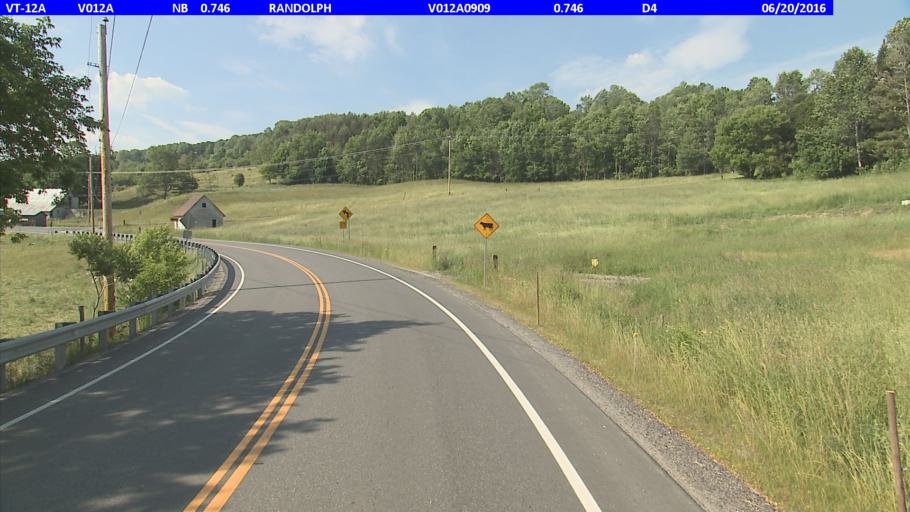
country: US
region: Vermont
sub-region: Orange County
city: Randolph
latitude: 43.9299
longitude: -72.6784
